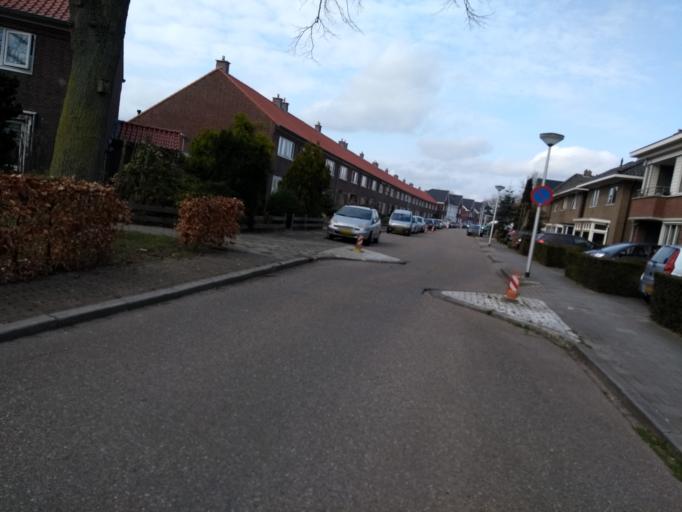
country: NL
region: Overijssel
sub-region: Gemeente Almelo
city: Almelo
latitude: 52.3448
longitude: 6.6769
